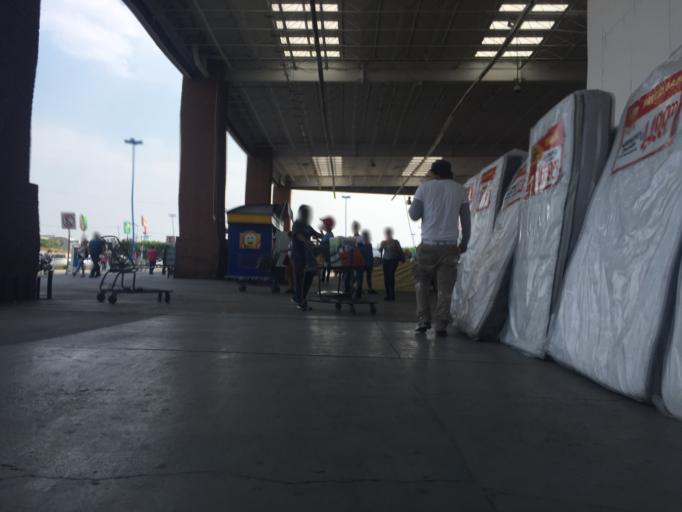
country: MX
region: Mexico City
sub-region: Iztacalco
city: Iztacalco
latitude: 19.3840
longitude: -99.0799
